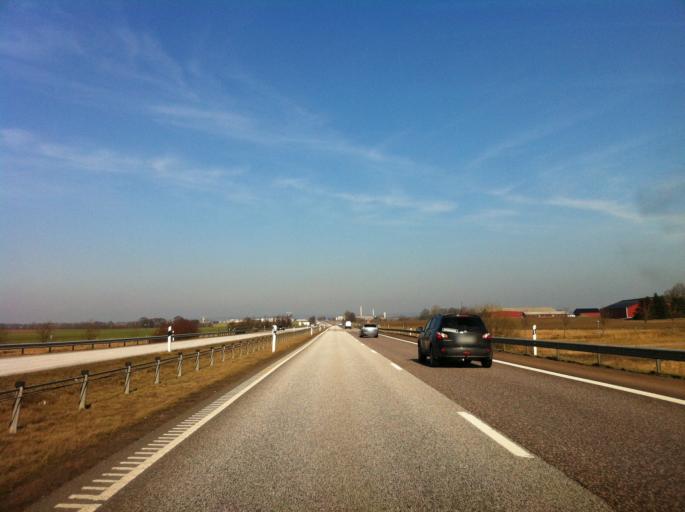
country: SE
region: Skane
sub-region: Angelholms Kommun
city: AEngelholm
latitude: 56.2261
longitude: 12.8978
